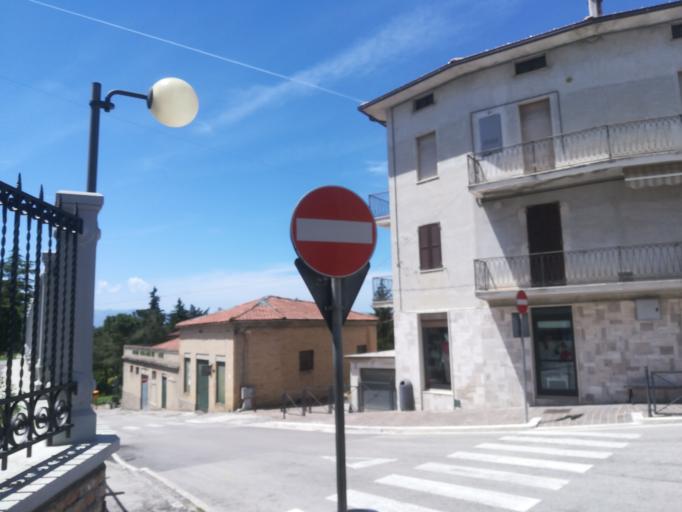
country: IT
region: The Marches
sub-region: Provincia di Macerata
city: Mogliano
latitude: 43.1857
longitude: 13.4763
